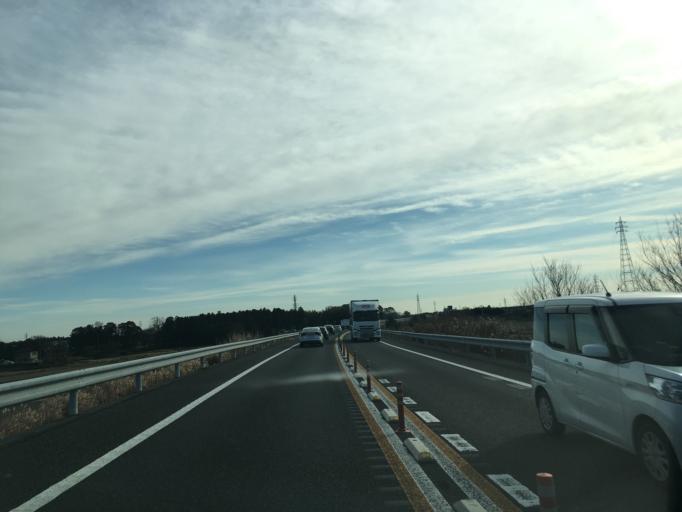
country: JP
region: Ibaraki
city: Naka
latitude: 36.0520
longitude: 140.1036
